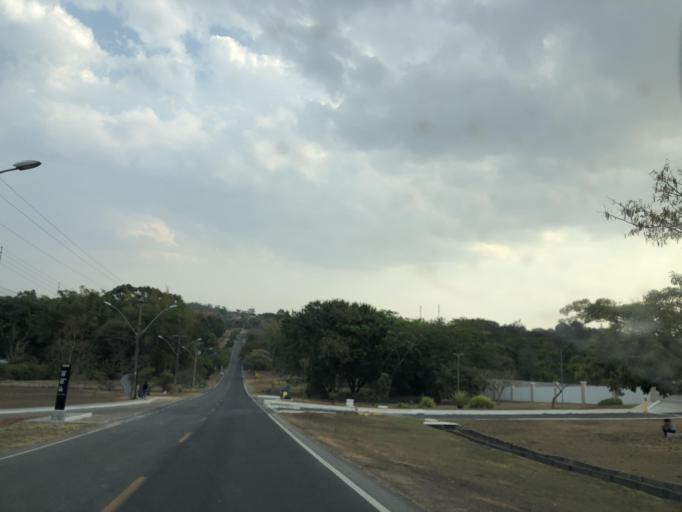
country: BR
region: Federal District
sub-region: Brasilia
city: Brasilia
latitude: -15.9335
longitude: -47.9737
